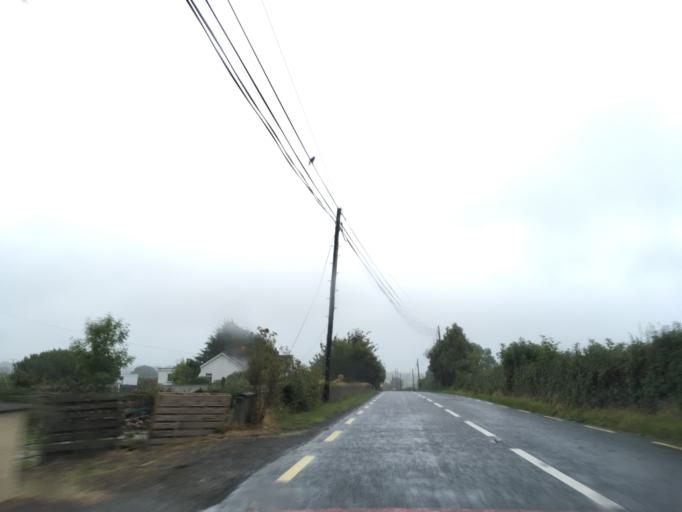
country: IE
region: Munster
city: Tipperary
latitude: 52.4831
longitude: -8.0817
